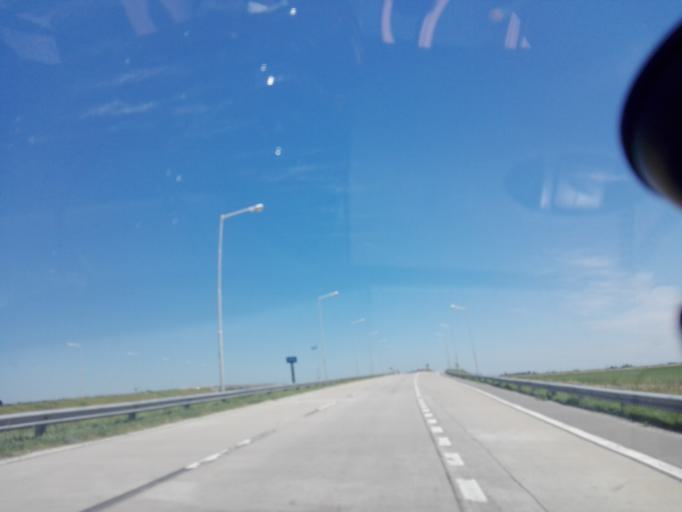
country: AR
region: Cordoba
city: Leones
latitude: -32.6389
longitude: -62.2395
